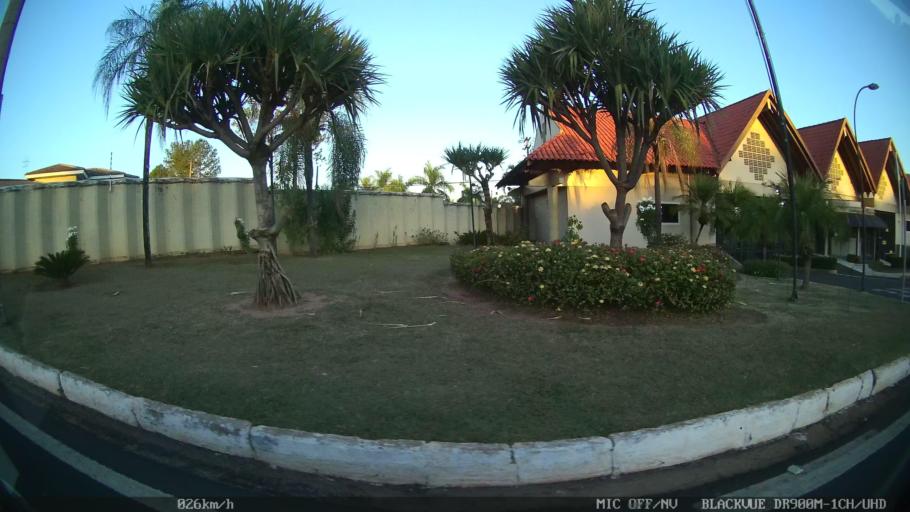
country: BR
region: Sao Paulo
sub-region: Sao Jose Do Rio Preto
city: Sao Jose do Rio Preto
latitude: -20.8621
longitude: -49.4092
